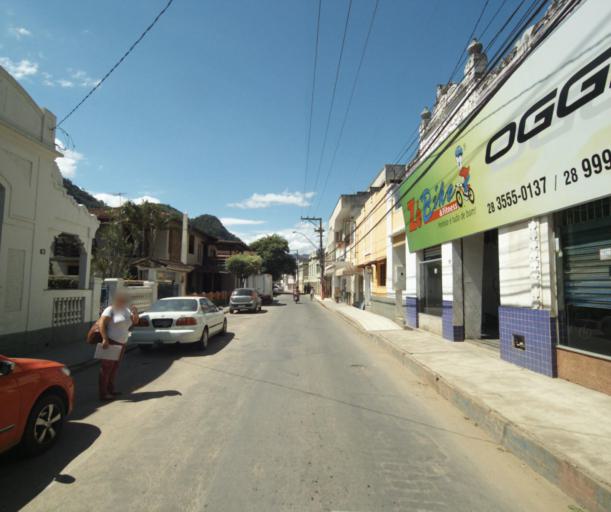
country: BR
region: Espirito Santo
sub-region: Mimoso Do Sul
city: Mimoso do Sul
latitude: -21.0620
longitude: -41.3623
